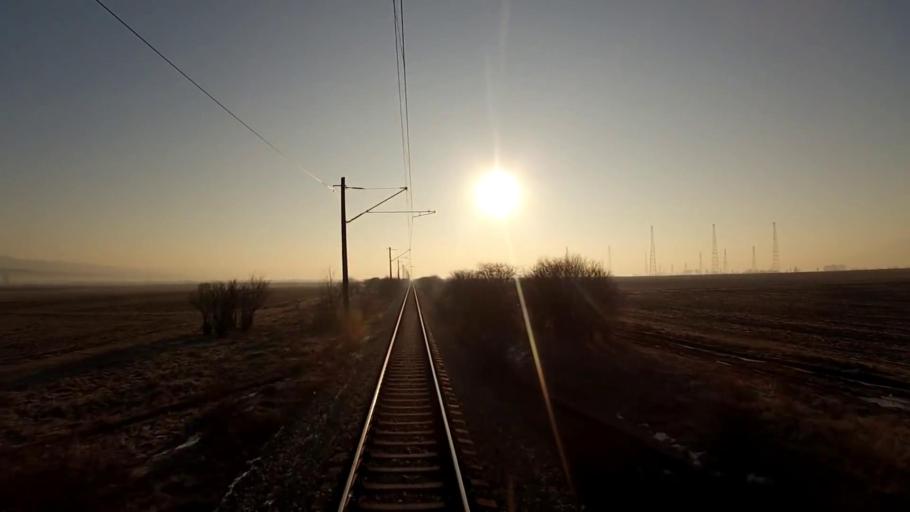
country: BG
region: Sofiya
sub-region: Obshtina Kostinbrod
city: Kostinbrod
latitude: 42.8131
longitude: 23.1894
